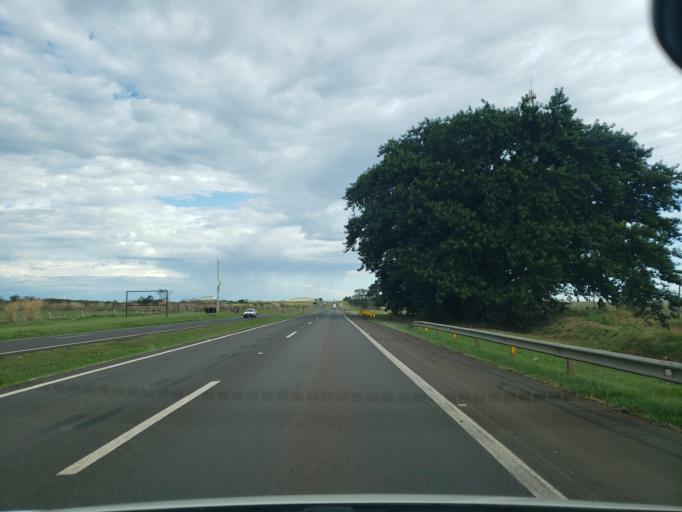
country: BR
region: Sao Paulo
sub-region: Jau
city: Jau
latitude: -22.2679
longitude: -48.4968
